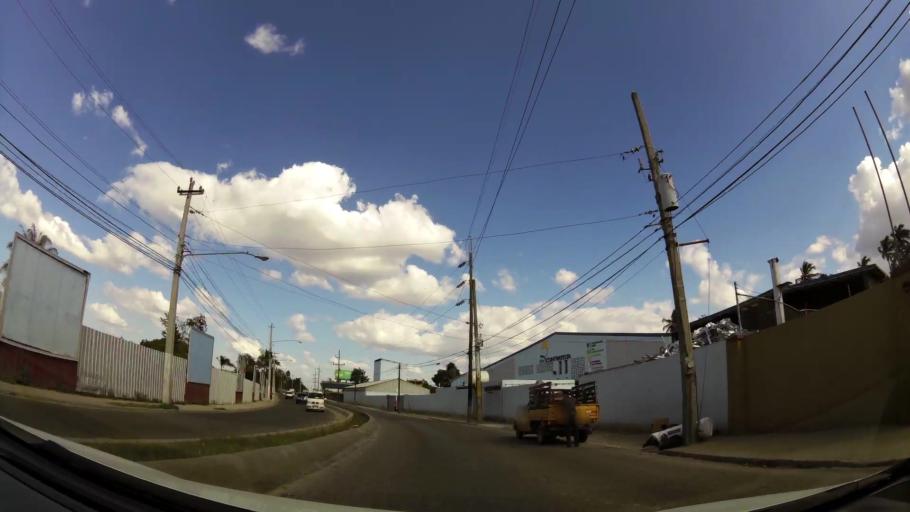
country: DO
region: Nacional
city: Santo Domingo
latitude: 18.5074
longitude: -69.9938
